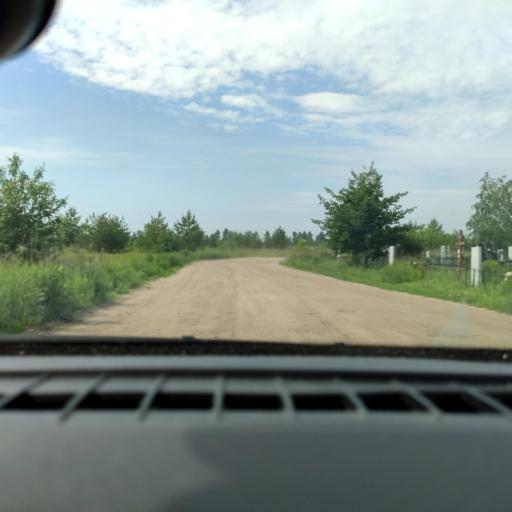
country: RU
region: Voronezj
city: Maslovka
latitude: 51.5085
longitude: 39.2100
